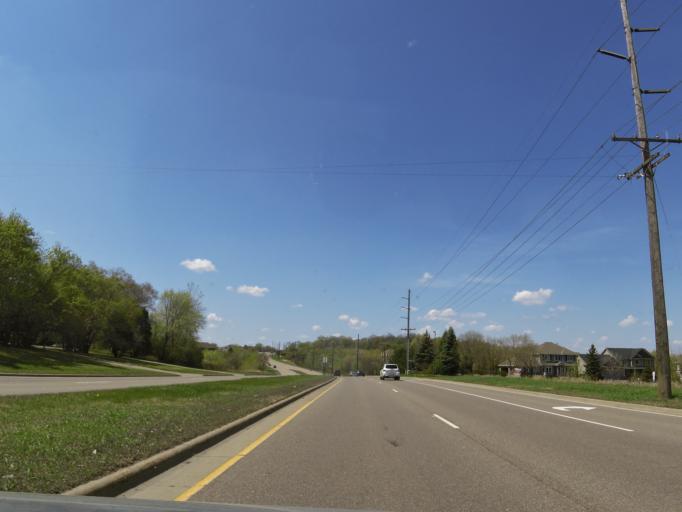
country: US
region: Minnesota
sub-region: Scott County
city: Savage
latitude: 44.7468
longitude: -93.3676
